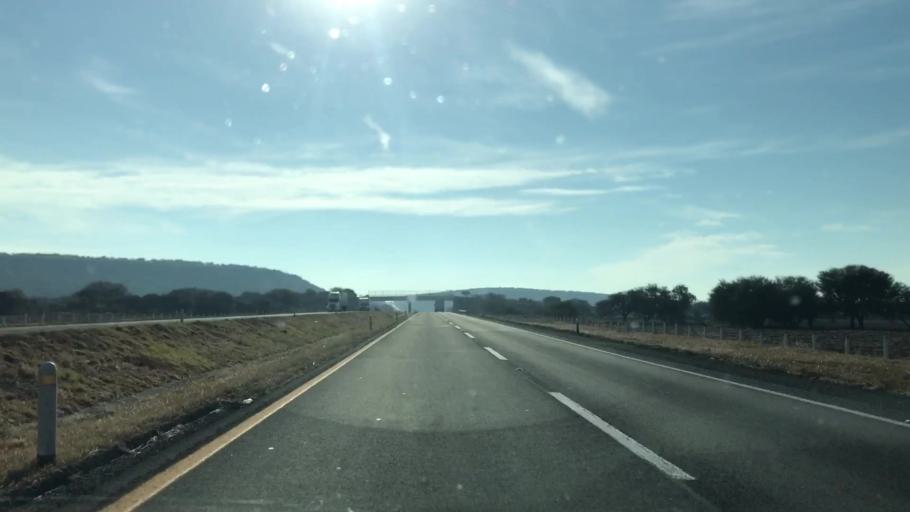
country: MX
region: Guanajuato
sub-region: Purisima del Rincon
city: Potrerillos (Guanajal)
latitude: 21.1509
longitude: -101.8458
